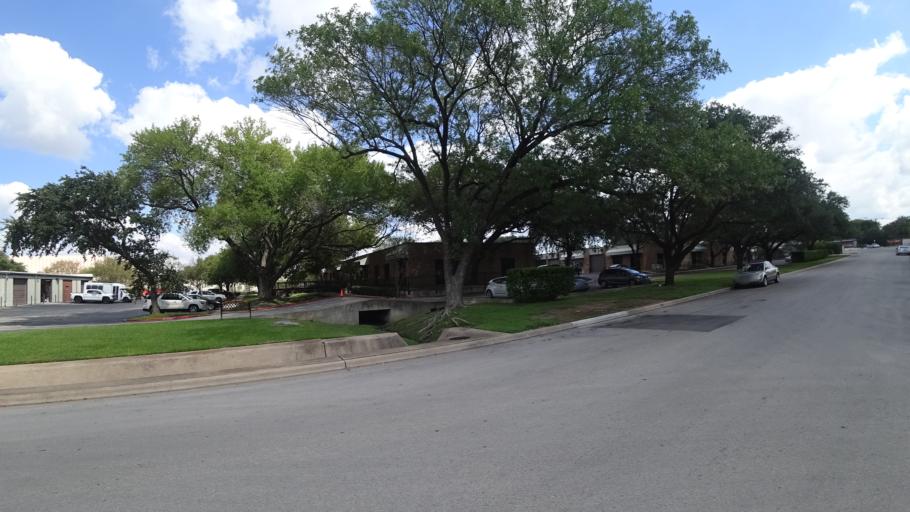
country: US
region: Texas
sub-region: Williamson County
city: Jollyville
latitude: 30.3684
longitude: -97.7256
